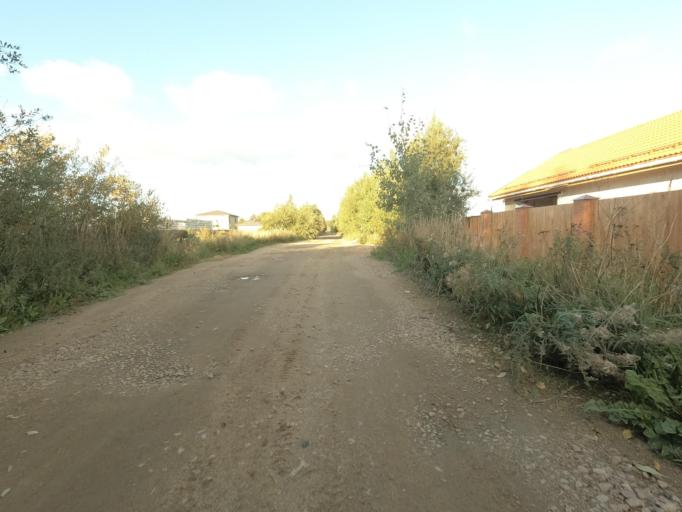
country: RU
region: Leningrad
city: Otradnoye
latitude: 59.8688
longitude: 30.7723
